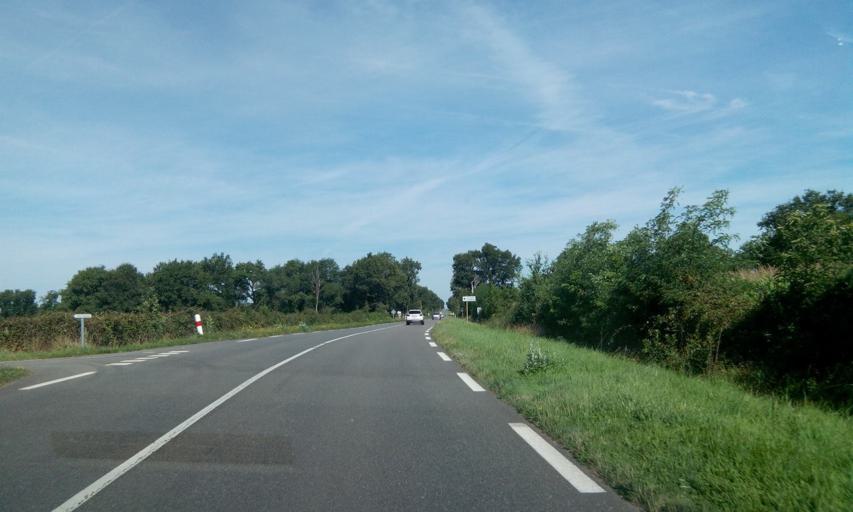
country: FR
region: Poitou-Charentes
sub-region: Departement de la Charente
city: Confolens
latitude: 46.0404
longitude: 0.6292
